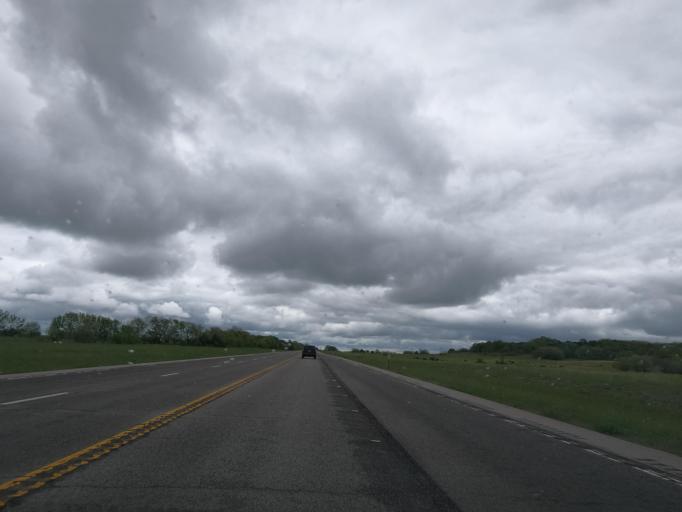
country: US
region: Kansas
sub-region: Montgomery County
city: Cherryvale
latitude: 37.3469
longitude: -95.4808
